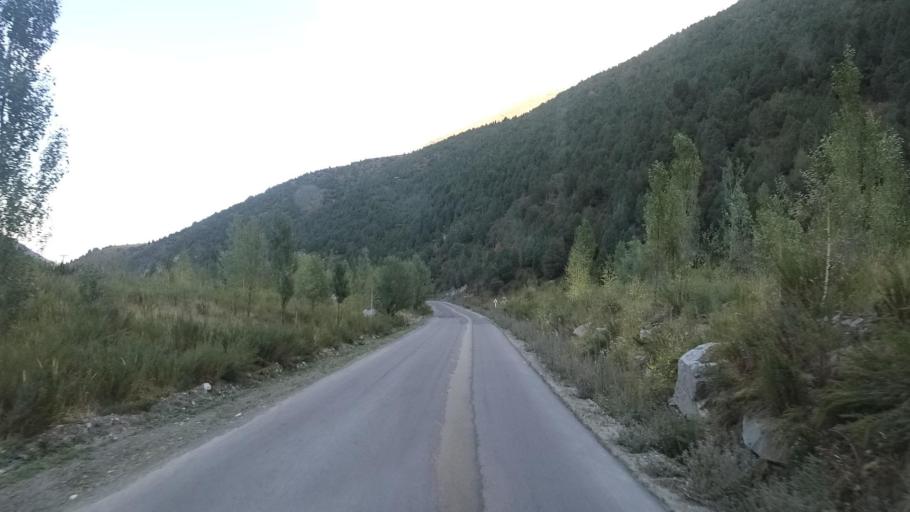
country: KG
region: Chuy
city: Bishkek
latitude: 42.6057
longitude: 74.4833
